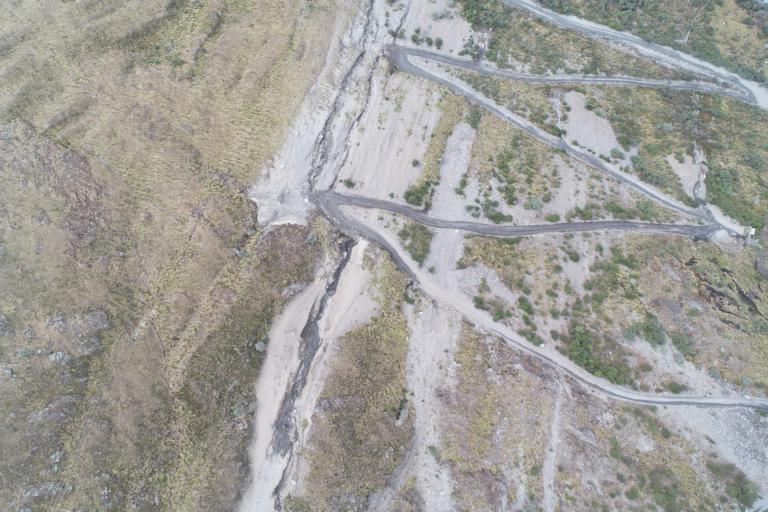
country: BO
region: La Paz
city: Sorata
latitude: -15.6553
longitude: -68.5329
